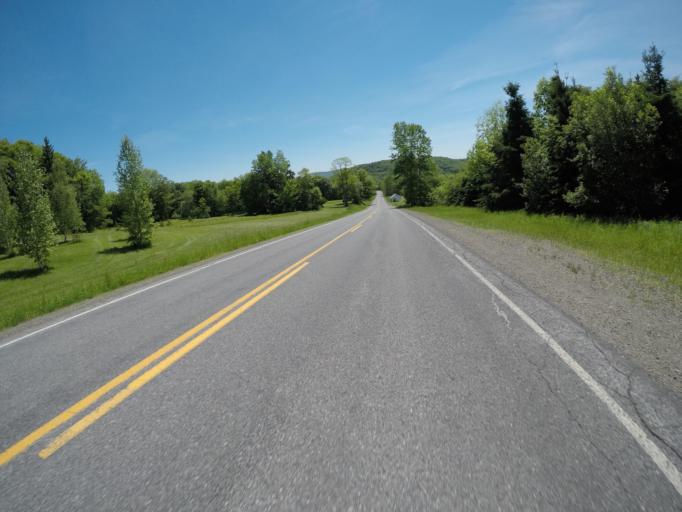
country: US
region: New York
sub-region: Delaware County
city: Delhi
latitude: 42.1975
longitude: -74.8414
